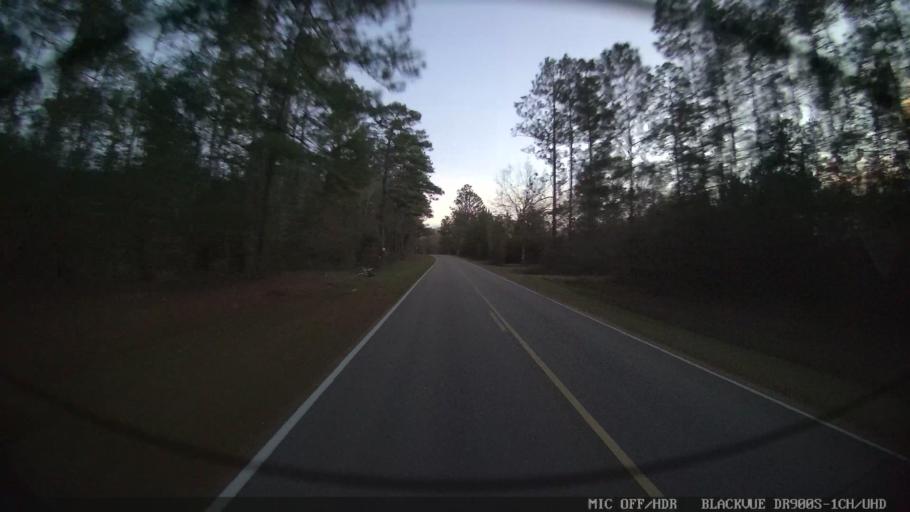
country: US
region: Mississippi
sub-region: Perry County
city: New Augusta
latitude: 31.1131
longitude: -89.1960
